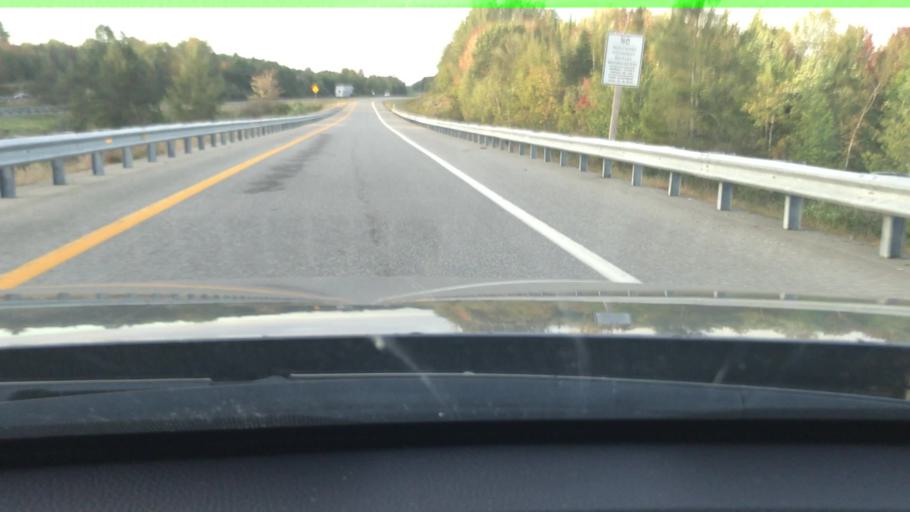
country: US
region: Maine
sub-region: Sagadahoc County
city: Richmond
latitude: 44.0997
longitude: -69.8714
